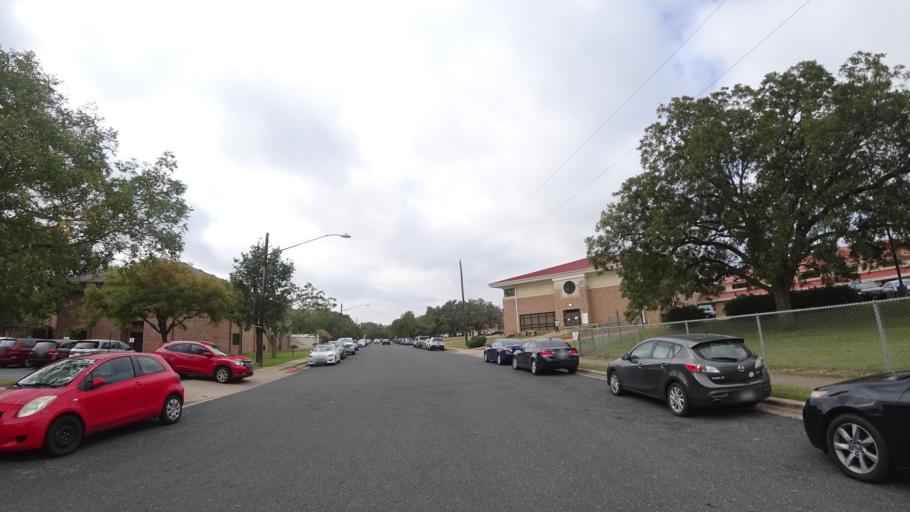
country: US
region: Texas
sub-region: Travis County
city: Shady Hollow
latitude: 30.2130
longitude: -97.8331
